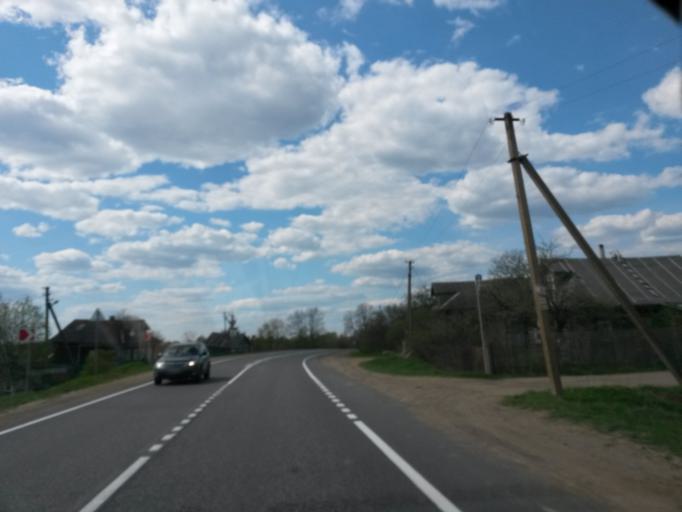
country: RU
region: Jaroslavl
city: Bol'shoye Selo
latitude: 57.7146
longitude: 39.1226
